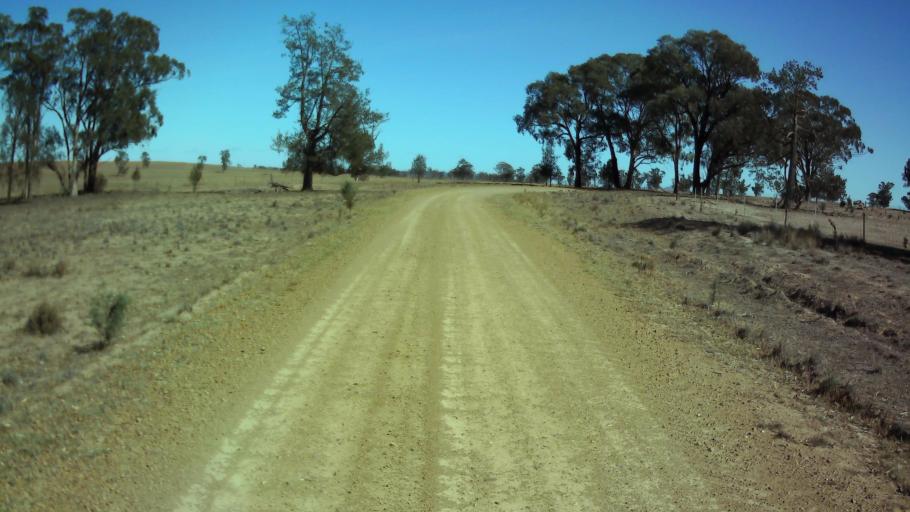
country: AU
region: New South Wales
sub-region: Weddin
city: Grenfell
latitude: -33.7584
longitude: 147.9204
